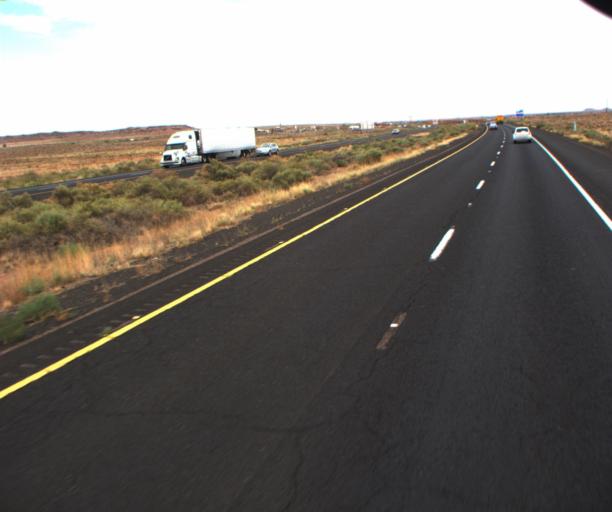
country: US
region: Arizona
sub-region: Navajo County
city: Holbrook
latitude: 34.9119
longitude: -110.2421
